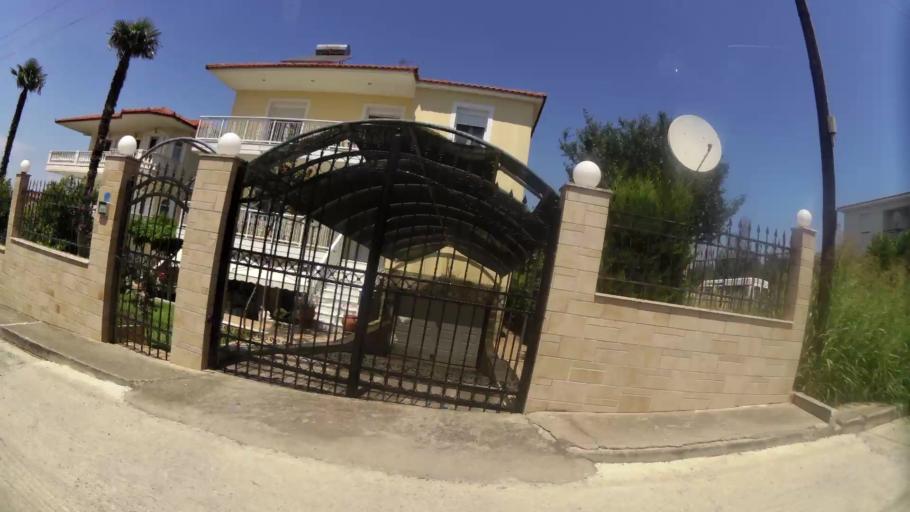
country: GR
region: Central Macedonia
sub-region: Nomos Thessalonikis
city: Nea Michaniona
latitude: 40.4760
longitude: 22.8668
